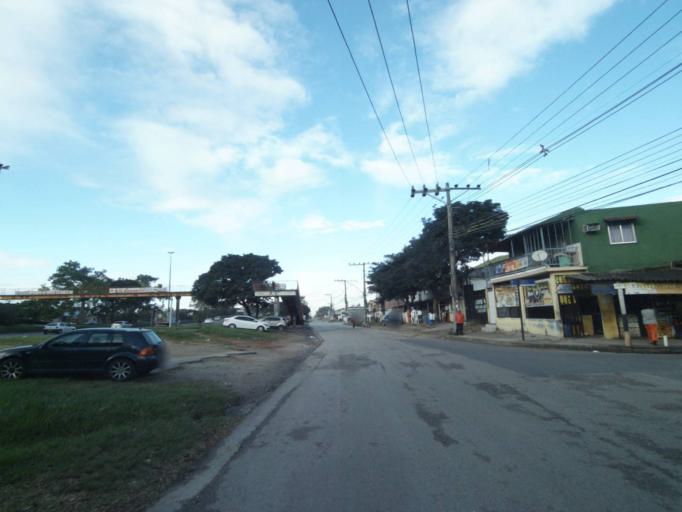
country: BR
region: Rio de Janeiro
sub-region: Nilopolis
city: Nilopolis
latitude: -22.8556
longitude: -43.4827
